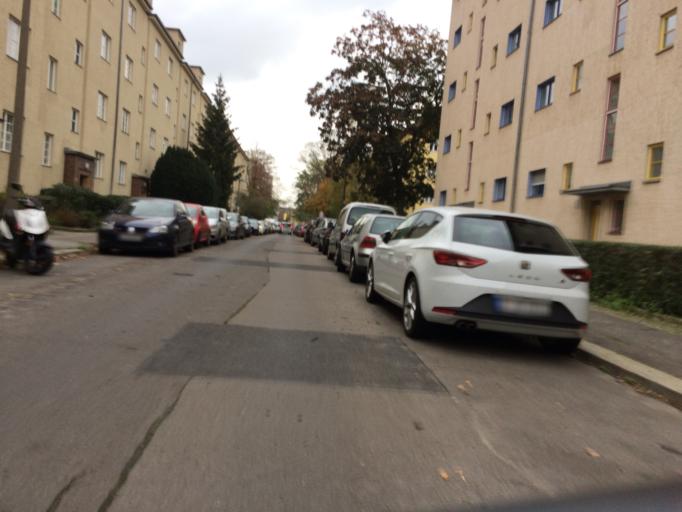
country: DE
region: Berlin
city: Prenzlauer Berg Bezirk
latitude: 52.5477
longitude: 13.4320
